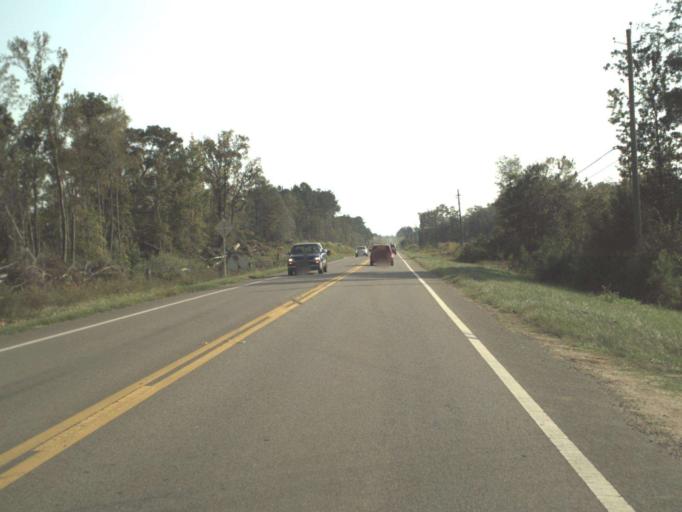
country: US
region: Florida
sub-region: Holmes County
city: Bonifay
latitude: 30.5871
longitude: -85.7983
